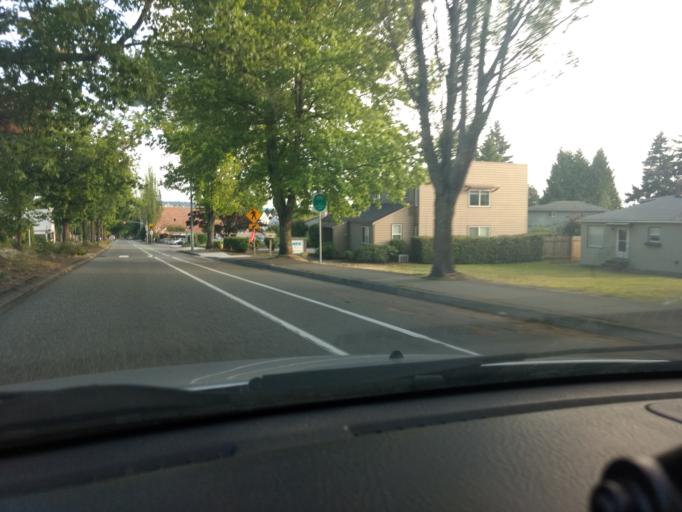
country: US
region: Washington
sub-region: King County
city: Kirkland
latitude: 47.6823
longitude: -122.2097
